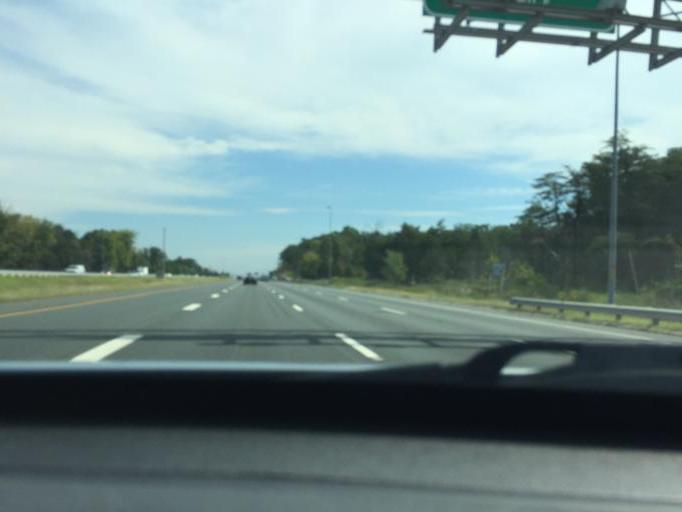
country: US
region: Virginia
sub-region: Prince William County
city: Bull Run
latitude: 38.7998
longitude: -77.5413
